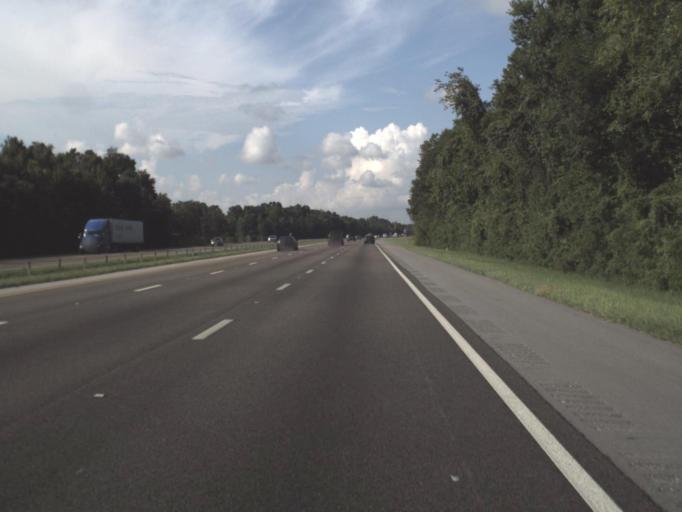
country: US
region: Florida
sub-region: Hillsborough County
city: Lutz
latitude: 28.1419
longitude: -82.4106
